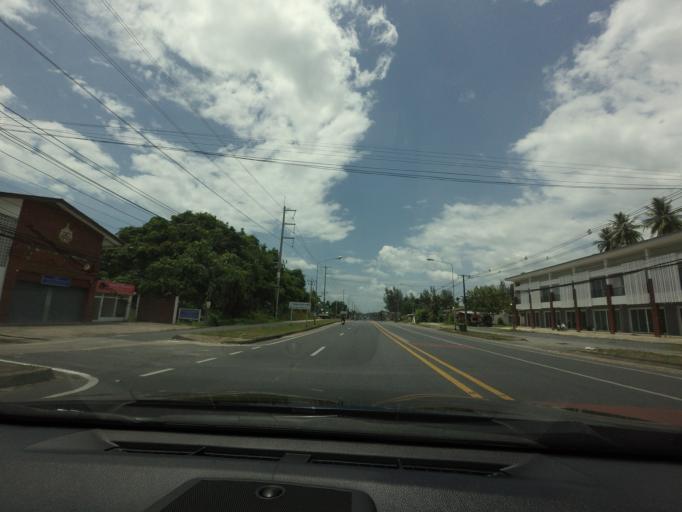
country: TH
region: Phangnga
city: Ban Khao Lak
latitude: 8.6588
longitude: 98.2533
